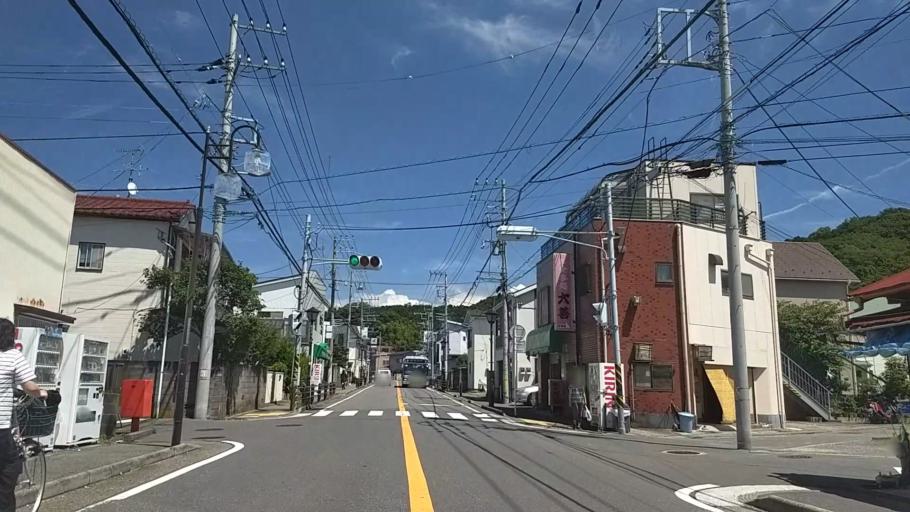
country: JP
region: Kanagawa
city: Zushi
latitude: 35.2954
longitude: 139.5854
